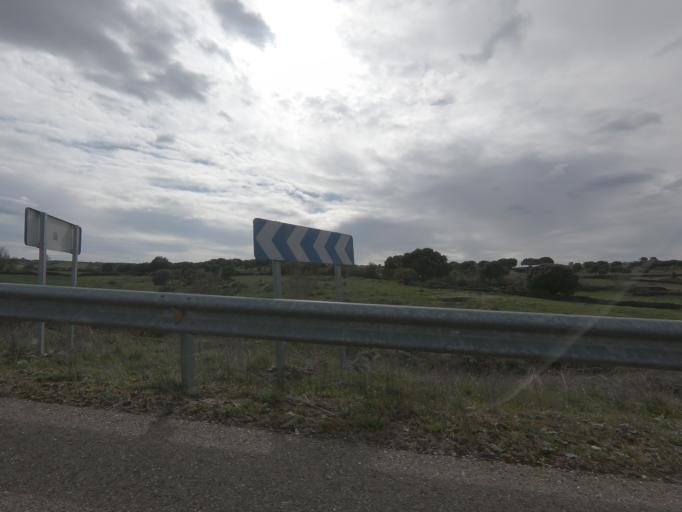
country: ES
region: Castille and Leon
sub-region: Provincia de Salamanca
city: Herguijuela de Ciudad Rodrigo
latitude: 40.4865
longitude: -6.5825
